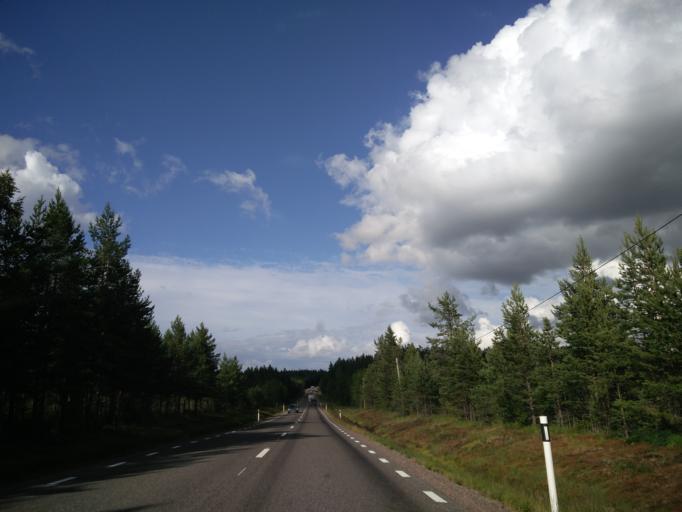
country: SE
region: Vaermland
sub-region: Torsby Kommun
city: Torsby
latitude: 60.3681
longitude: 13.1990
